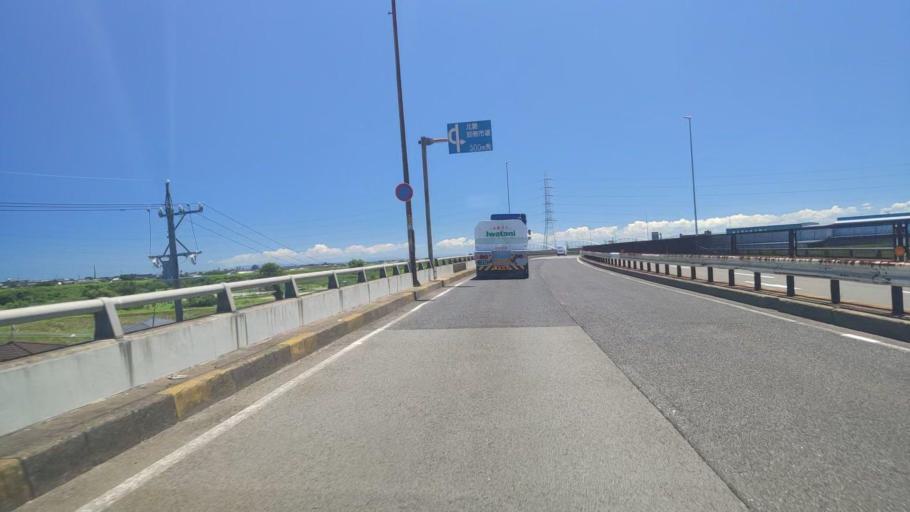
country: JP
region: Mie
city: Yokkaichi
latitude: 34.9257
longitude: 136.6153
